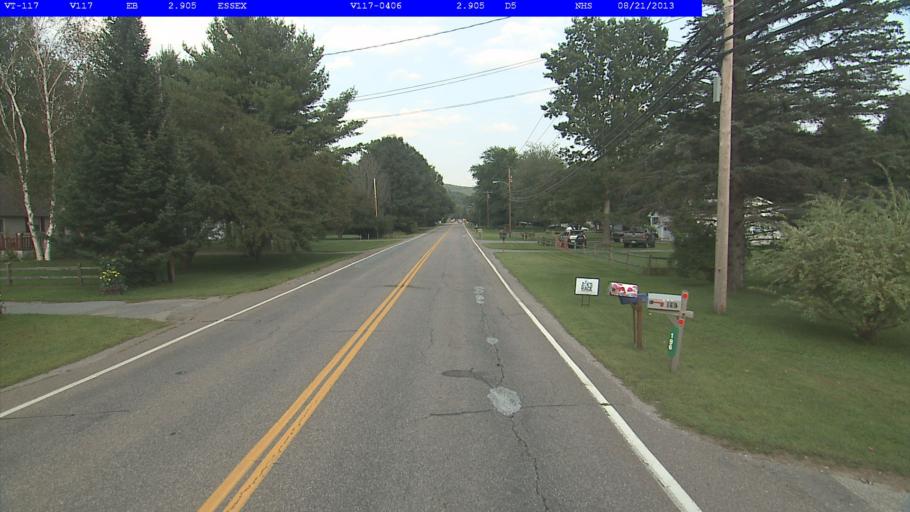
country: US
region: Vermont
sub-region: Chittenden County
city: Williston
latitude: 44.4790
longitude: -73.0568
